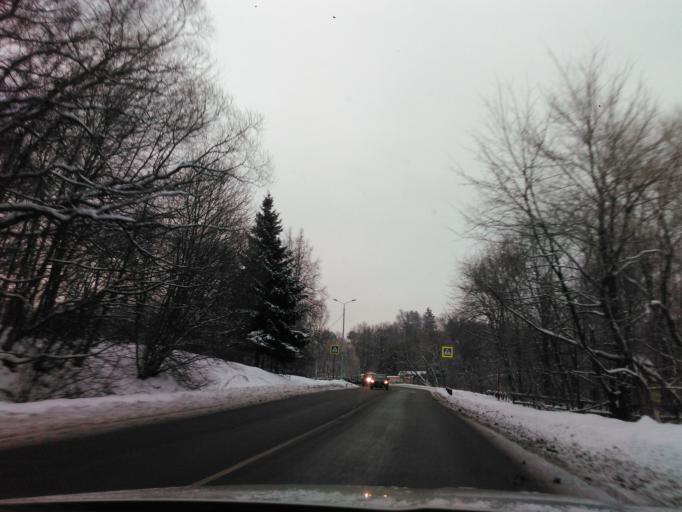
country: RU
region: Moscow
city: Khimki
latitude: 55.8877
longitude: 37.3790
